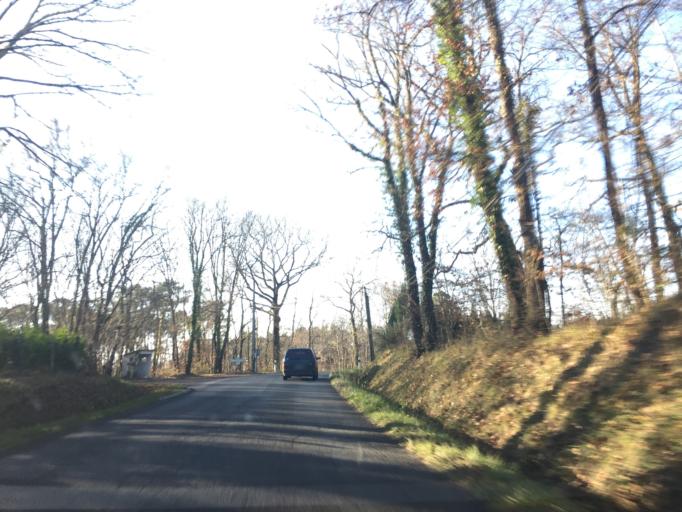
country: FR
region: Aquitaine
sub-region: Departement de la Dordogne
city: Neuvic
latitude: 45.1368
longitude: 0.4774
